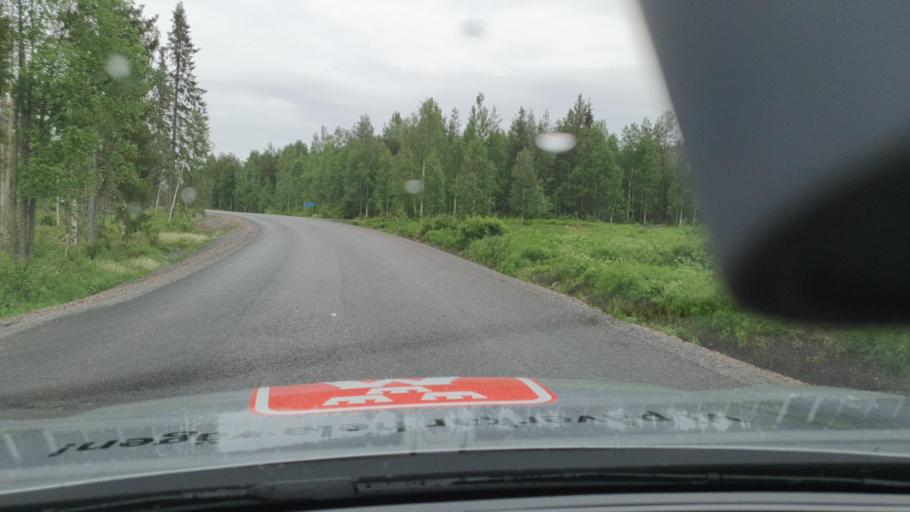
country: SE
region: Norrbotten
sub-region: Pajala Kommun
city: Pajala
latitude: 66.7364
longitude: 23.1692
